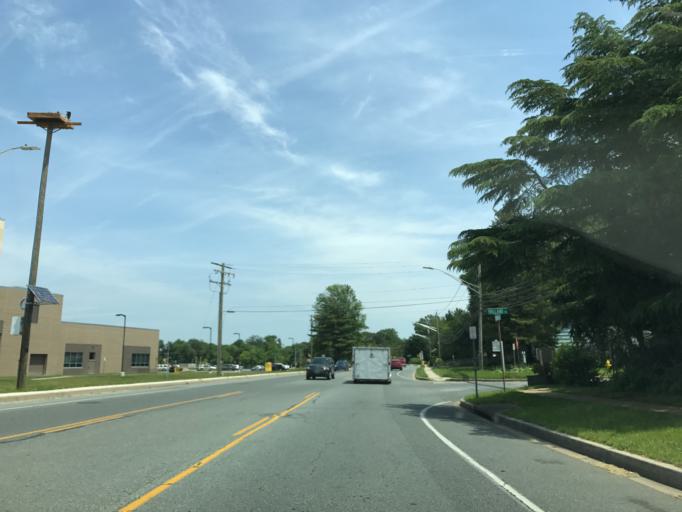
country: US
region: Maryland
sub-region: Anne Arundel County
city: Severna Park
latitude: 39.0761
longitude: -76.5619
